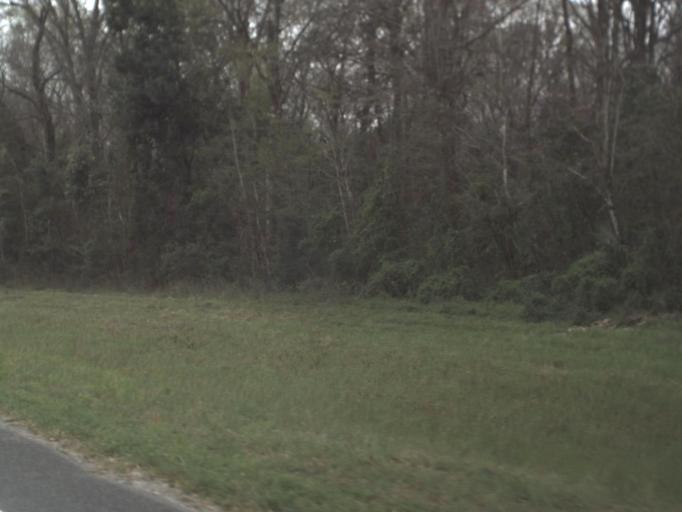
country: US
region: Florida
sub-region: Wakulla County
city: Crawfordville
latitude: 30.1487
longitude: -84.2849
